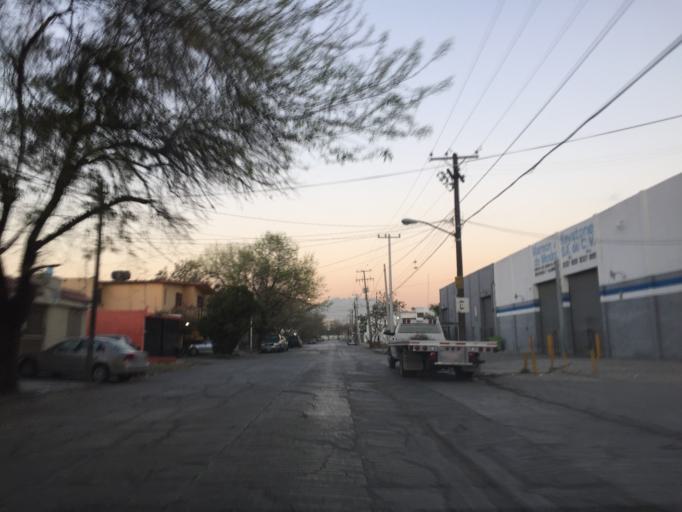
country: MX
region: Nuevo Leon
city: Guadalupe
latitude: 25.6994
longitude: -100.2198
